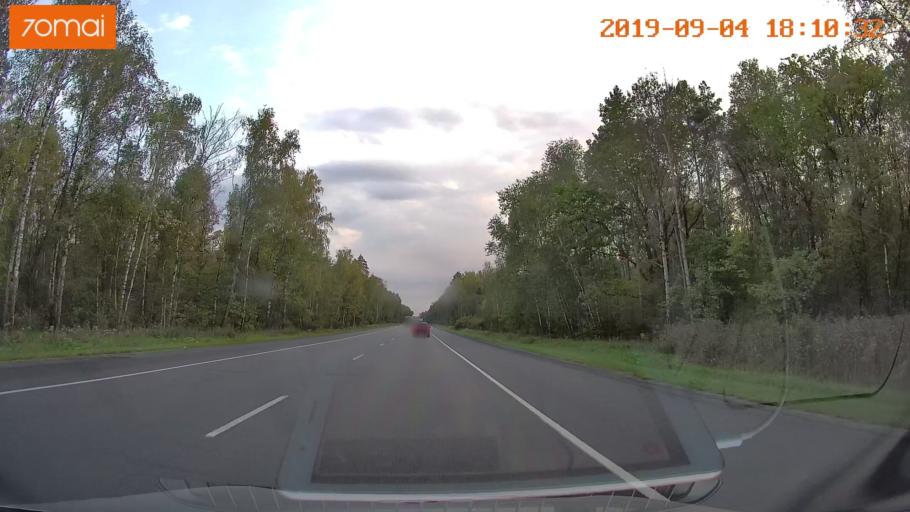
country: RU
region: Moskovskaya
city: Lopatinskiy
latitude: 55.3868
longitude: 38.7643
